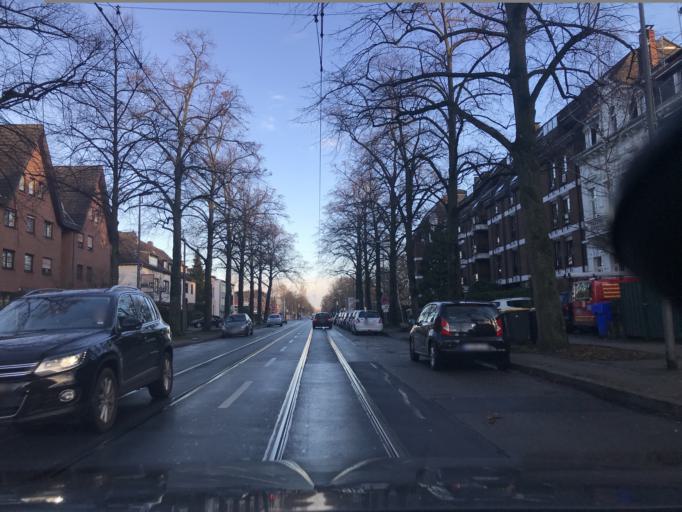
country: DE
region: North Rhine-Westphalia
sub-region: Regierungsbezirk Dusseldorf
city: Krefeld
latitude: 51.3407
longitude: 6.5959
